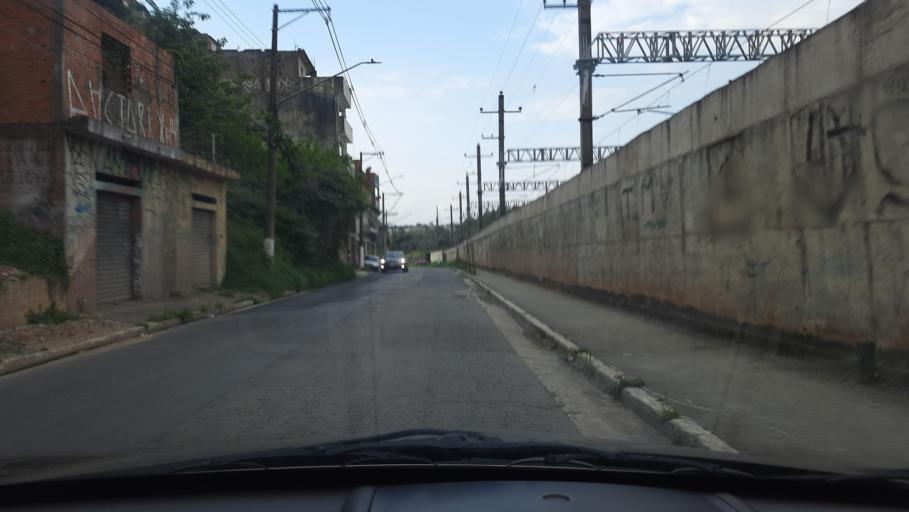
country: BR
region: Sao Paulo
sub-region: Caieiras
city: Caieiras
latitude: -23.4498
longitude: -46.7424
